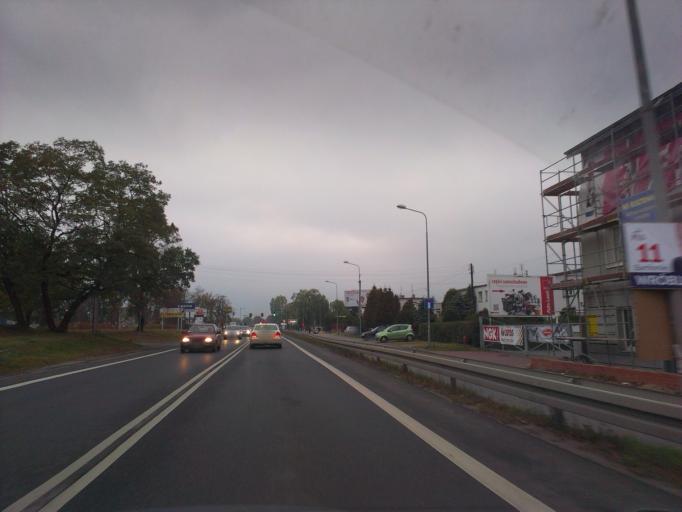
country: PL
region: Greater Poland Voivodeship
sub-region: Powiat poznanski
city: Suchy Las
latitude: 52.4747
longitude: 16.8747
